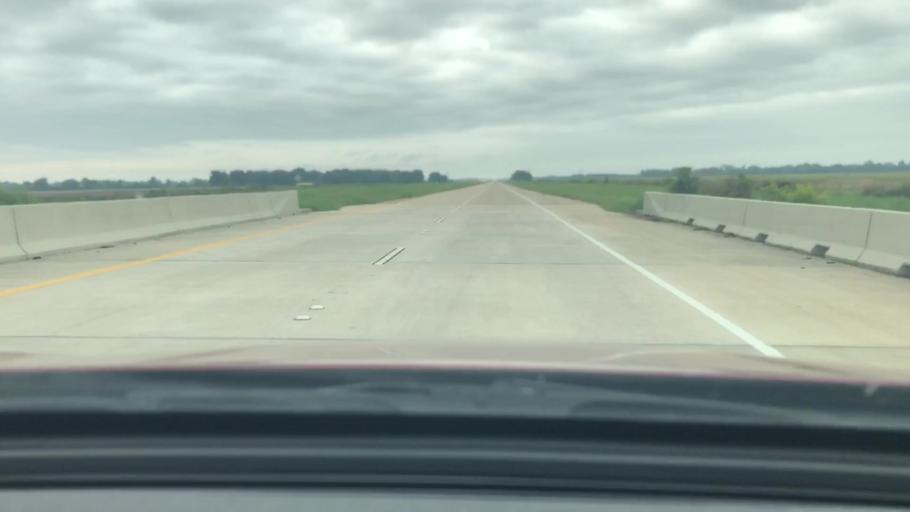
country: US
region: Louisiana
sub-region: Caddo Parish
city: Oil City
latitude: 32.7311
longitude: -93.8738
